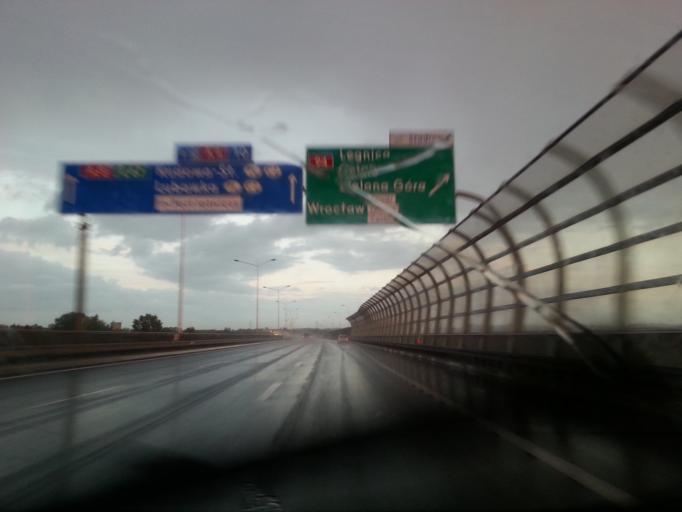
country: PL
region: Lower Silesian Voivodeship
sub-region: Powiat wroclawski
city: Smolec
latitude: 51.1367
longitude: 16.9366
